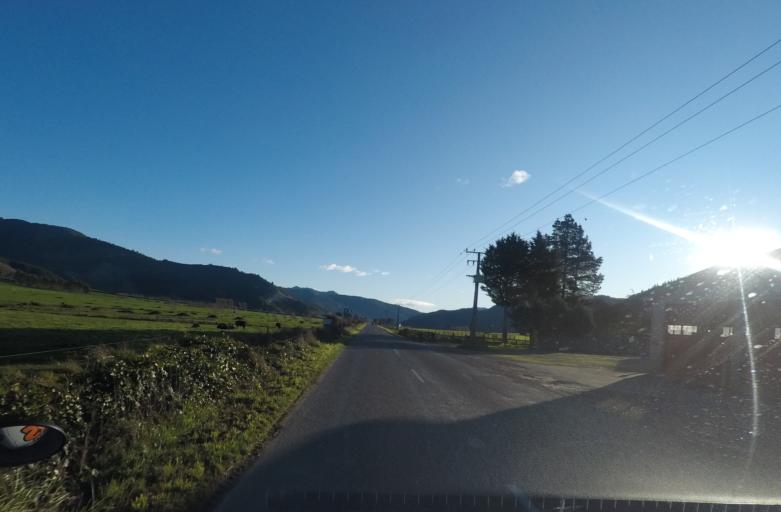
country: NZ
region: Marlborough
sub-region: Marlborough District
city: Picton
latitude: -41.2896
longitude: 173.8796
